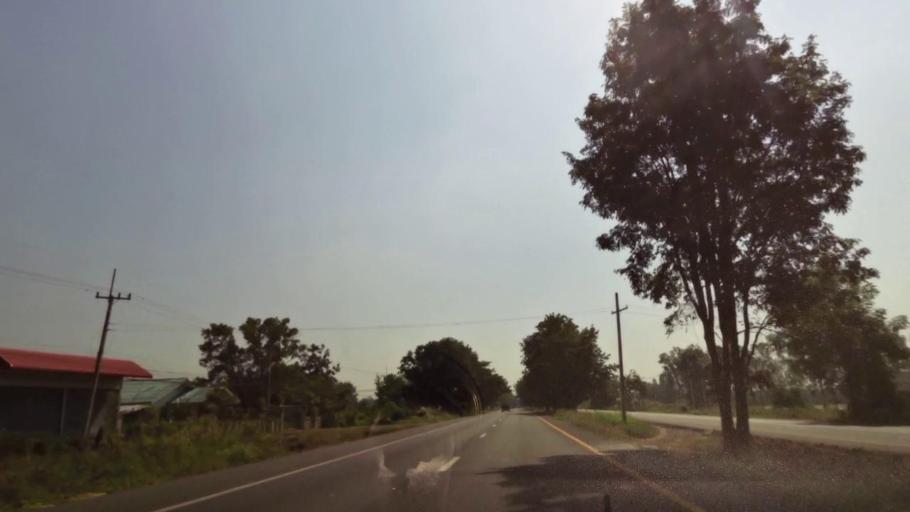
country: TH
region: Nakhon Sawan
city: Kao Liao
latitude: 15.9728
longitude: 100.1192
